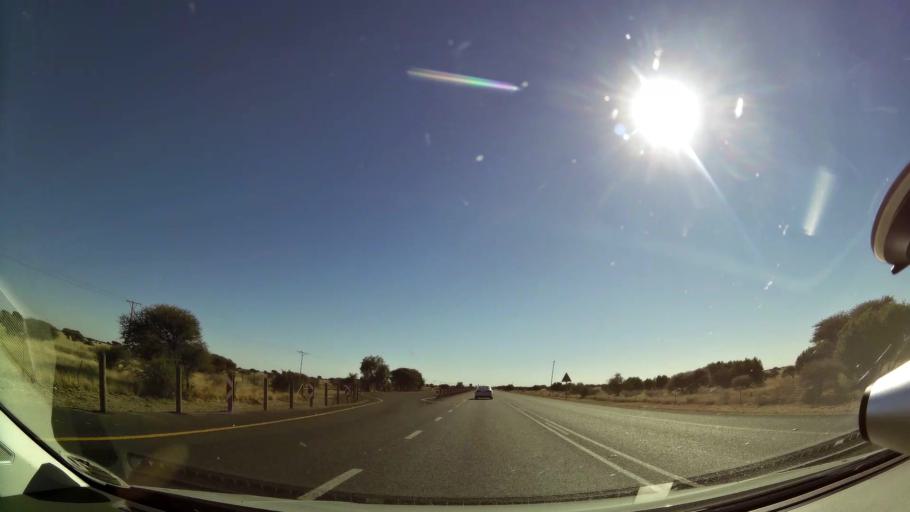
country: ZA
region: Northern Cape
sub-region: Frances Baard District Municipality
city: Warrenton
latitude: -28.1569
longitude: 24.8394
